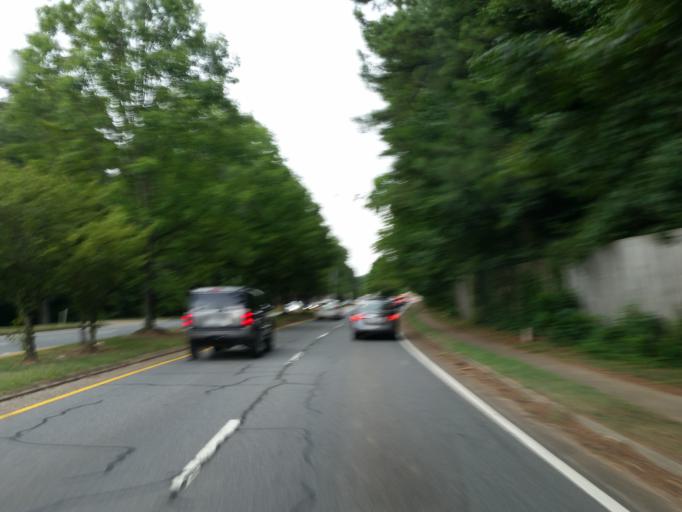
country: US
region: Georgia
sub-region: Fulton County
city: Roswell
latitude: 34.0622
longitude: -84.4295
